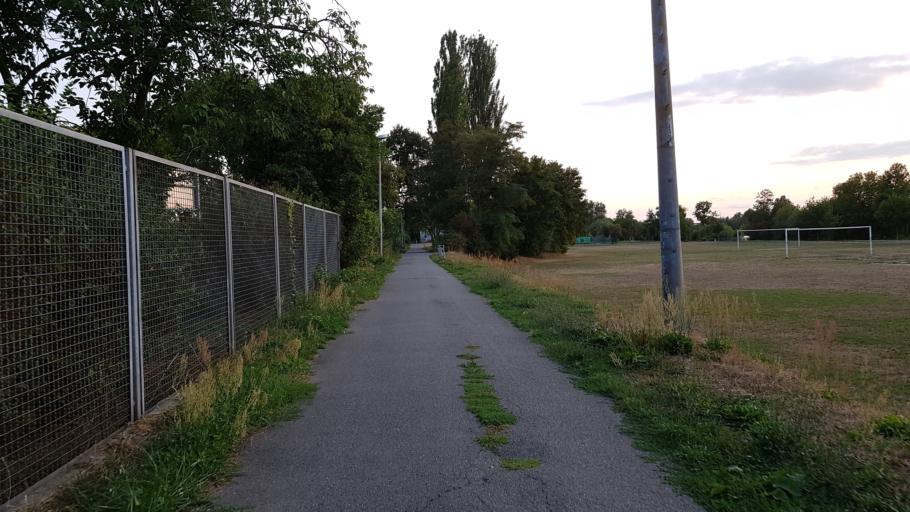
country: DE
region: Hesse
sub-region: Regierungsbezirk Darmstadt
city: Russelsheim
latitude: 50.0022
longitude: 8.4212
